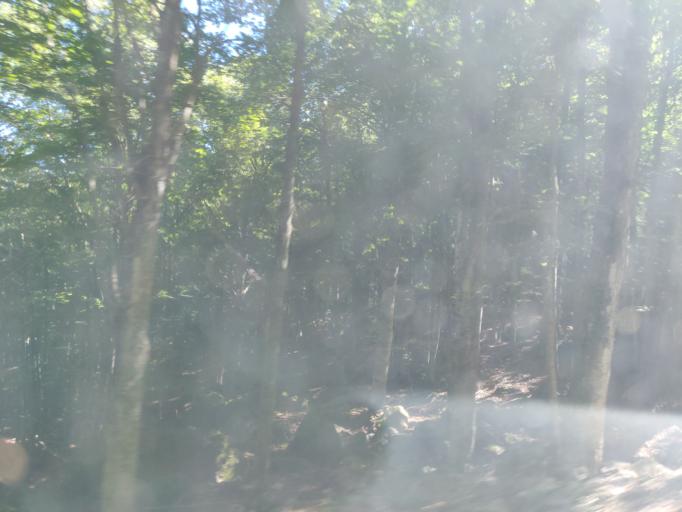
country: IT
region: Tuscany
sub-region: Provincia di Siena
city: Abbadia San Salvatore
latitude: 42.8922
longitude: 11.6324
